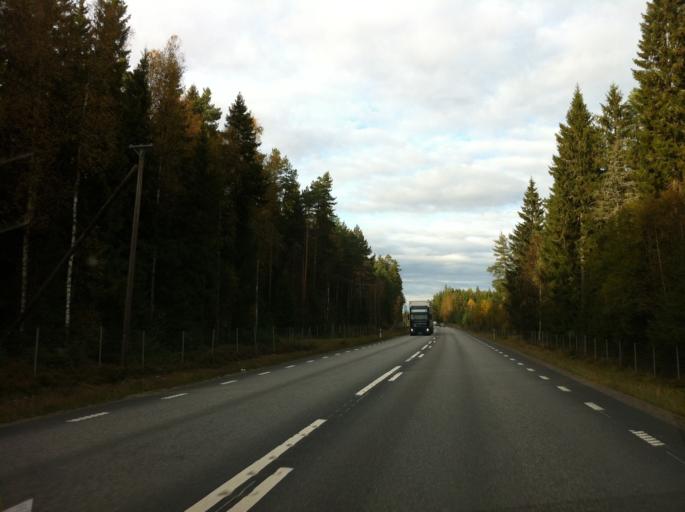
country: SE
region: OErebro
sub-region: Askersunds Kommun
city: Asbro
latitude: 58.9417
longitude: 15.0112
